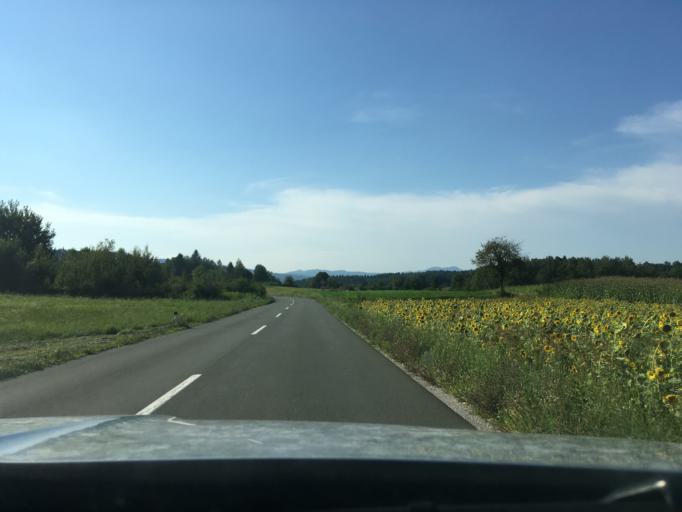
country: SI
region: Crnomelj
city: Crnomelj
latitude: 45.4862
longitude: 15.1953
